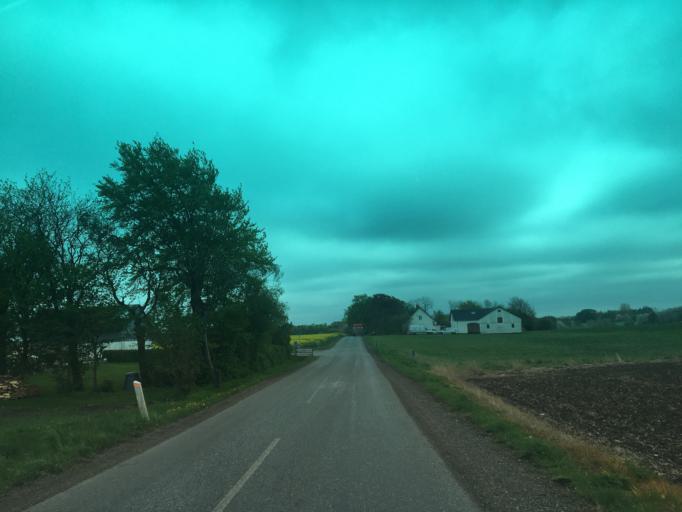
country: DK
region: Zealand
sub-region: Ringsted Kommune
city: Ringsted
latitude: 55.4174
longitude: 11.7078
